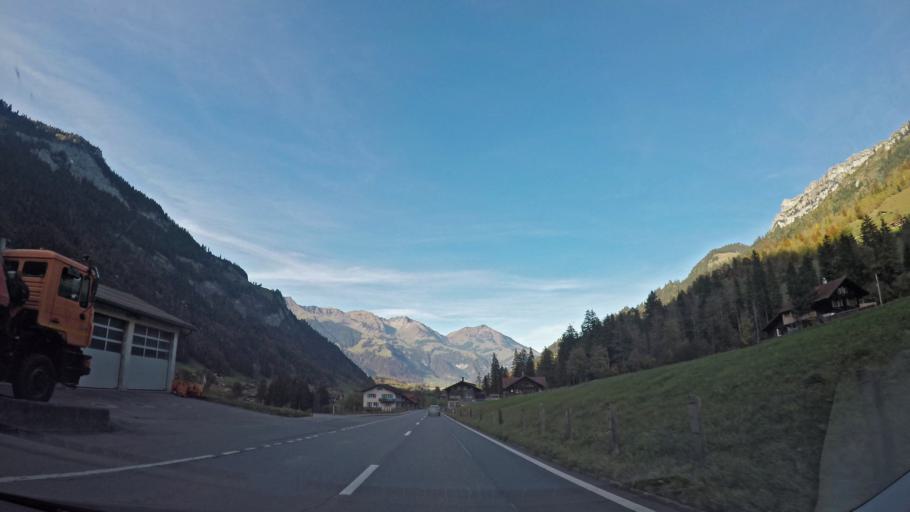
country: CH
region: Bern
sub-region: Frutigen-Niedersimmental District
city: Frutigen
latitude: 46.5479
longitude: 7.6611
